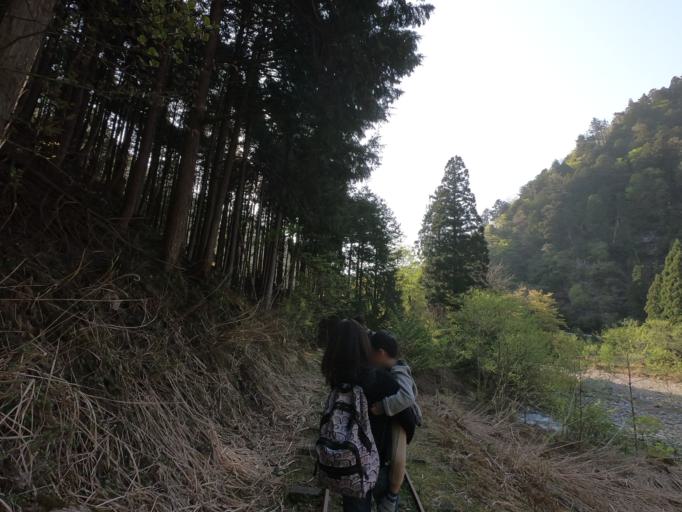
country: JP
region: Fukui
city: Obama
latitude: 35.3062
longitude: 135.7223
